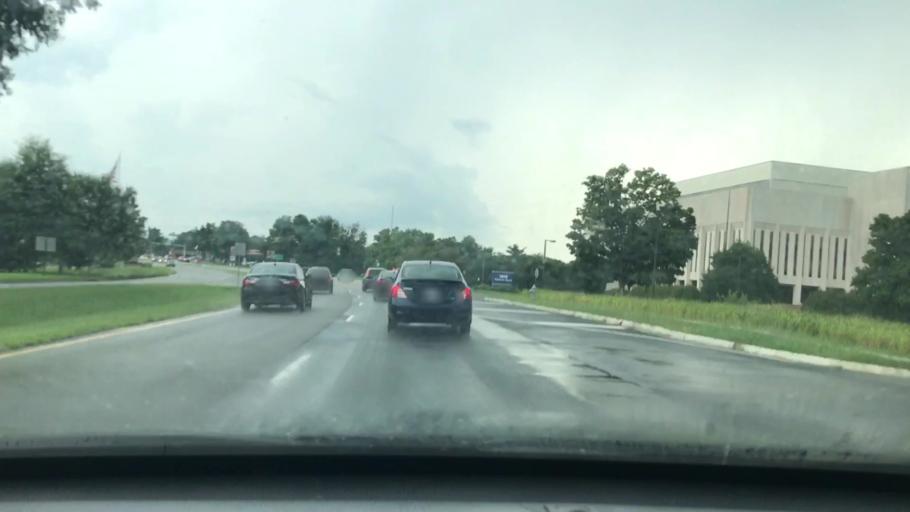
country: US
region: Virginia
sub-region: Henrico County
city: Laurel
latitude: 37.6311
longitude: -77.5318
